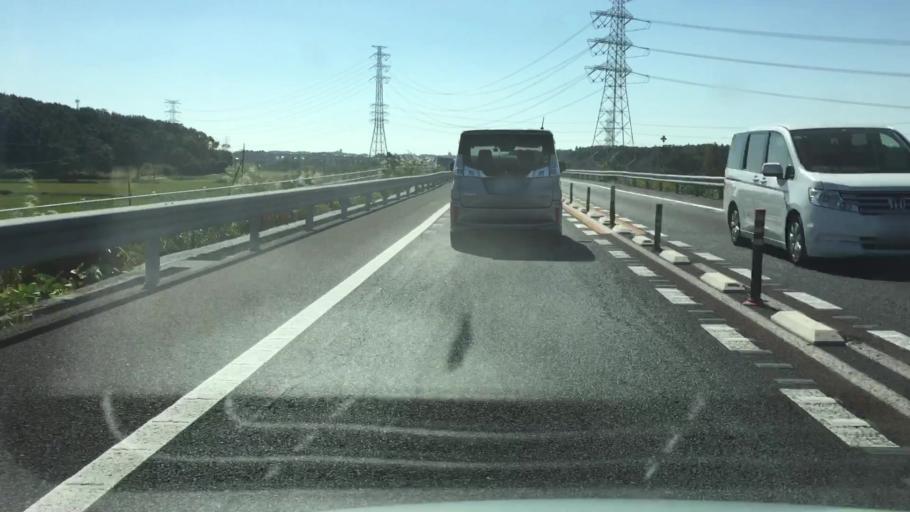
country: JP
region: Ibaraki
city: Ushiku
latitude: 36.0082
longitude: 140.1440
